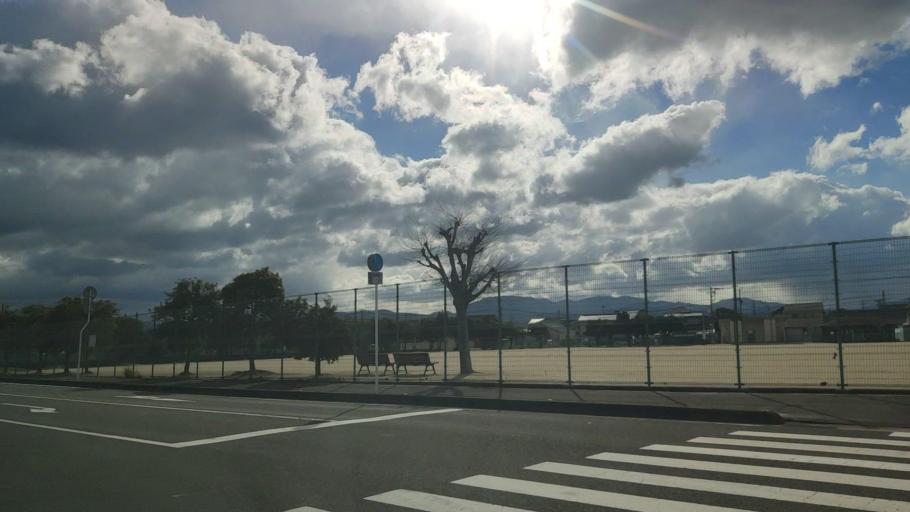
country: JP
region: Ehime
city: Masaki-cho
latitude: 33.8174
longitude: 132.7113
